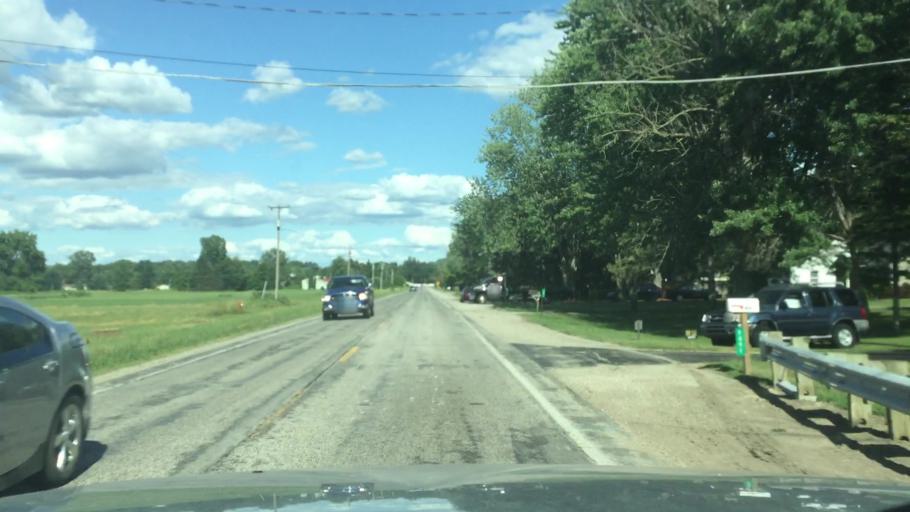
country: US
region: Michigan
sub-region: Saginaw County
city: Shields
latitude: 43.3792
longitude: -84.0618
